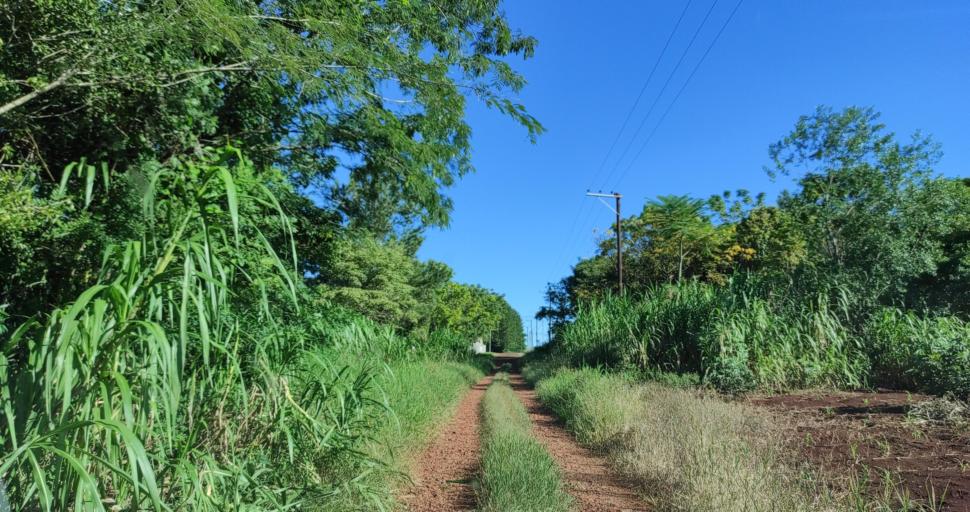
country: AR
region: Misiones
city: Capiovi
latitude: -26.9328
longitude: -55.0474
